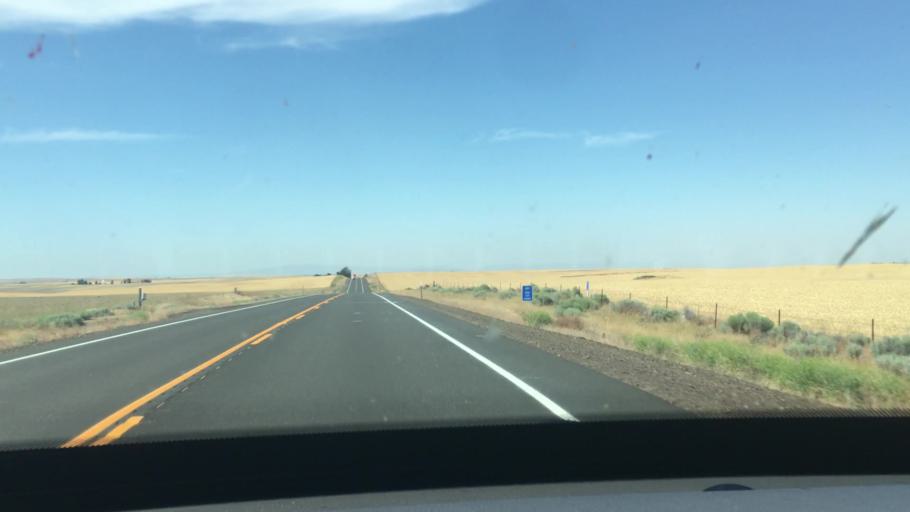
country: US
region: Oregon
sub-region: Sherman County
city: Moro
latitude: 45.3090
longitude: -120.7685
